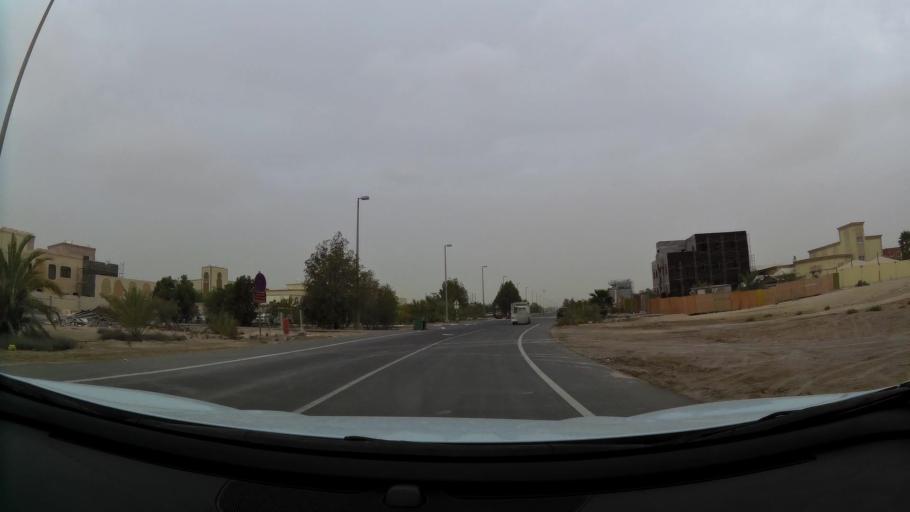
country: AE
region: Abu Dhabi
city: Abu Dhabi
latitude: 24.3777
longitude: 54.7025
